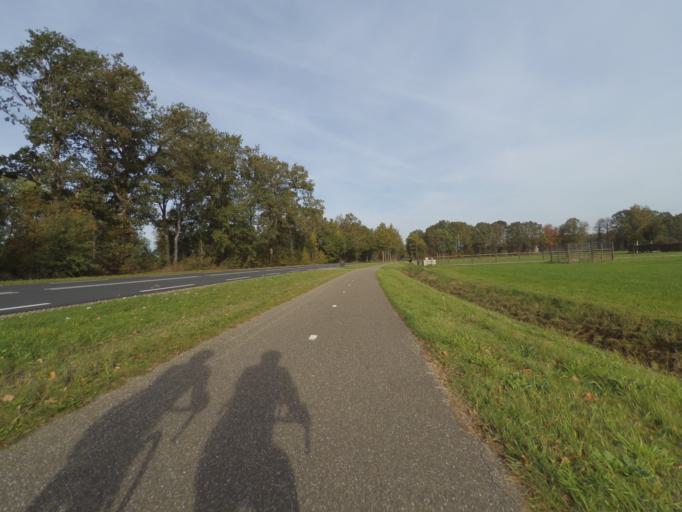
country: NL
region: Overijssel
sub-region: Gemeente Raalte
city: Raalte
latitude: 52.3508
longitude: 6.2729
